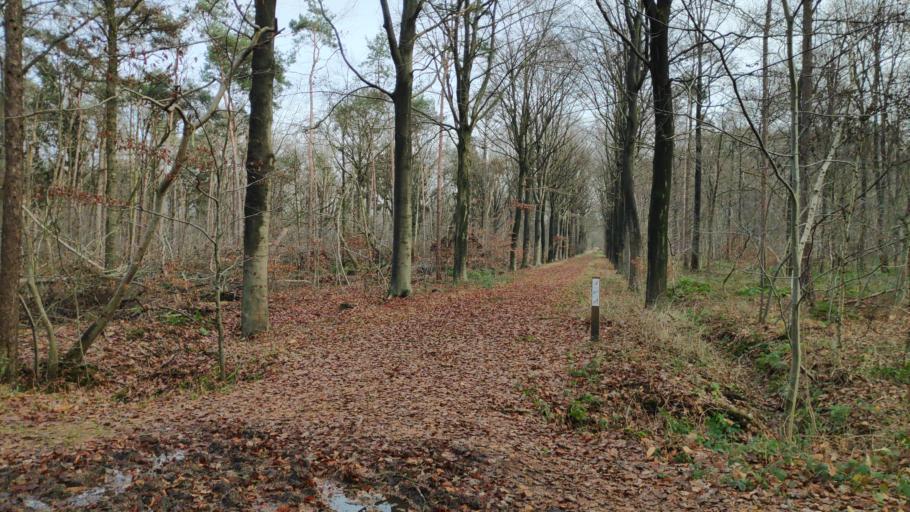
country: BE
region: Flanders
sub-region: Provincie Oost-Vlaanderen
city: Knesselare
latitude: 51.1555
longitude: 3.4419
